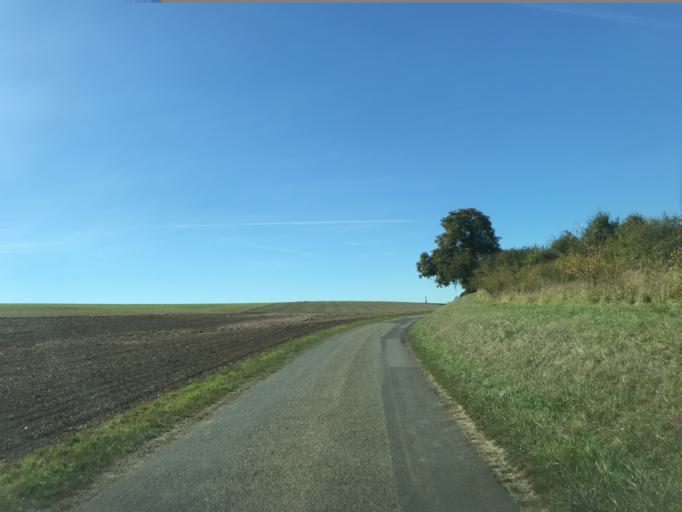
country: FR
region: Haute-Normandie
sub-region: Departement de l'Eure
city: Ande
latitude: 49.1742
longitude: 1.2661
